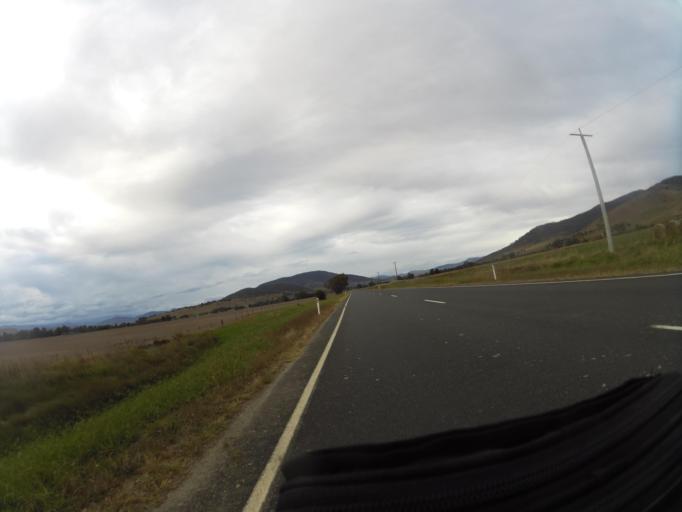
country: AU
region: New South Wales
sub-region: Snowy River
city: Jindabyne
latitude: -36.1033
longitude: 147.9806
